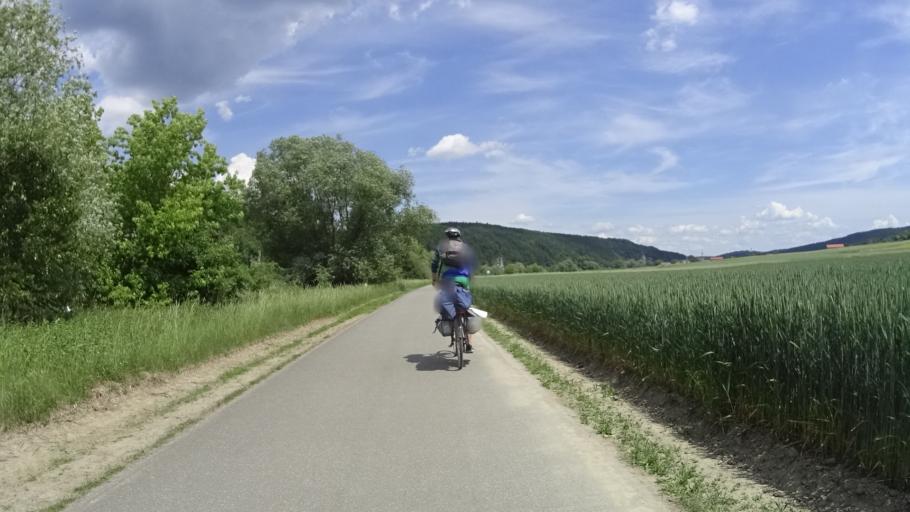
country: DE
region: Bavaria
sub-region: Lower Bavaria
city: Bad Abbach
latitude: 48.9585
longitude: 11.9899
